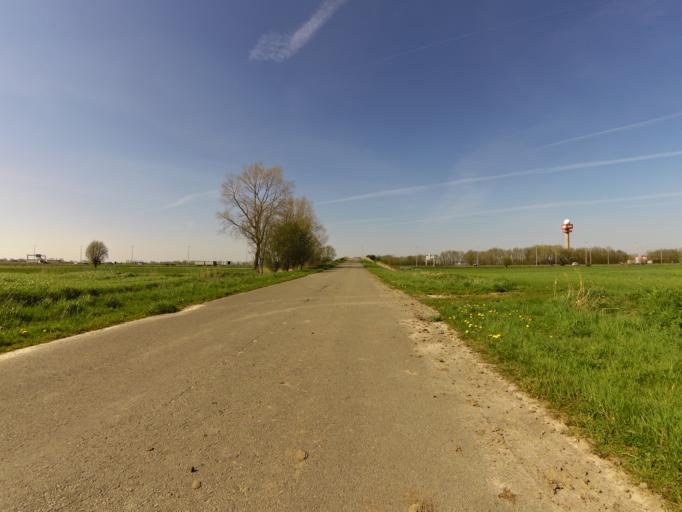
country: BE
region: Flanders
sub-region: Provincie West-Vlaanderen
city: Jabbeke
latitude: 51.1877
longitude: 3.0629
